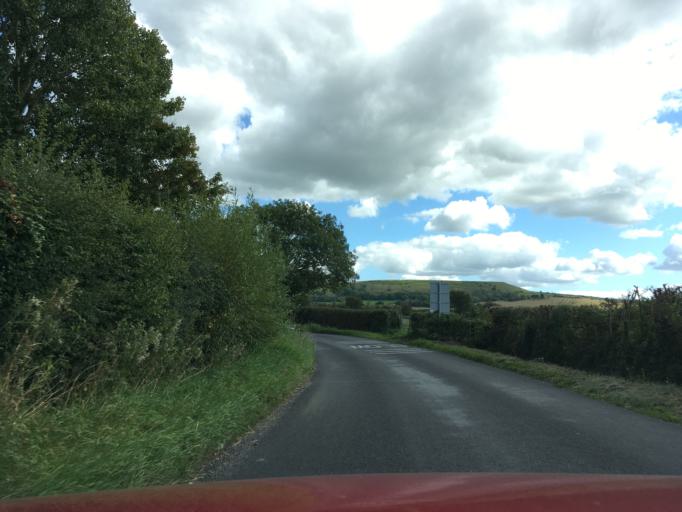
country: GB
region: England
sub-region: Wiltshire
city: Bratton
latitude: 51.2810
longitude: -2.1273
